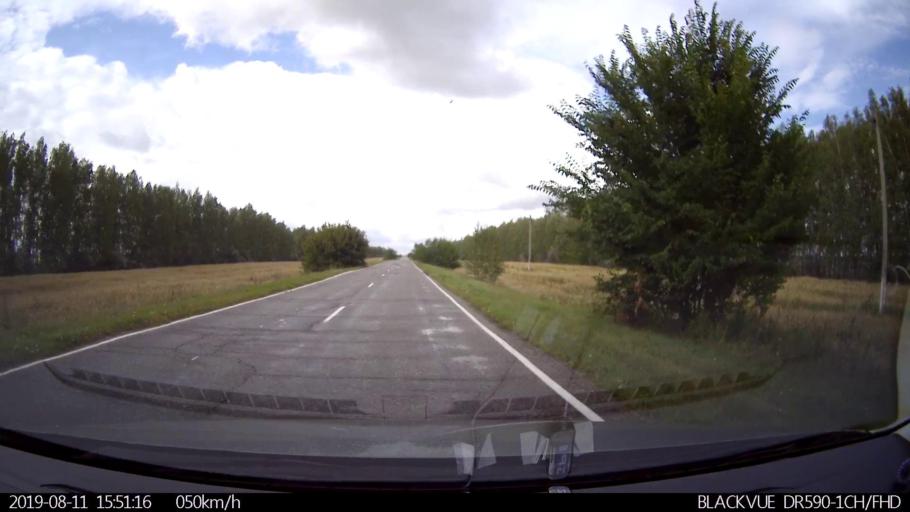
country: RU
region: Ulyanovsk
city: Ignatovka
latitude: 53.9175
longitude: 47.6560
